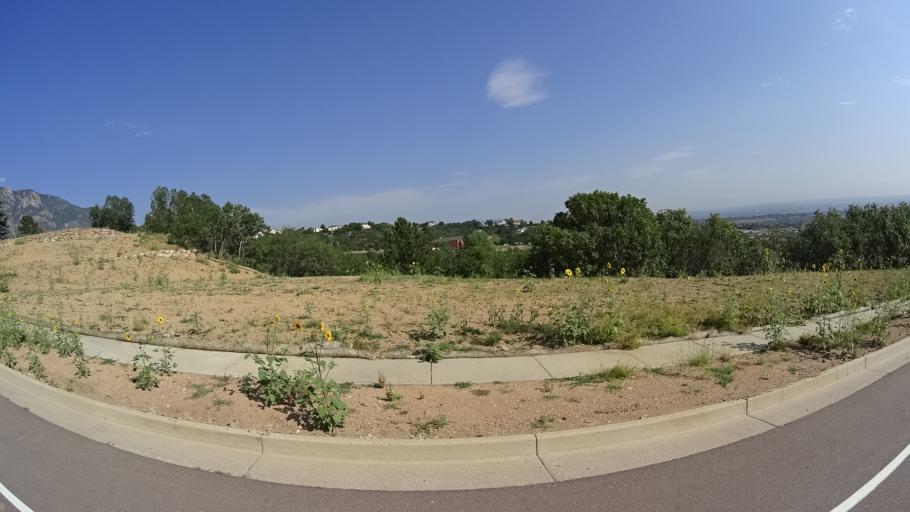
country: US
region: Colorado
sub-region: El Paso County
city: Fort Carson
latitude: 38.7572
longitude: -104.8221
